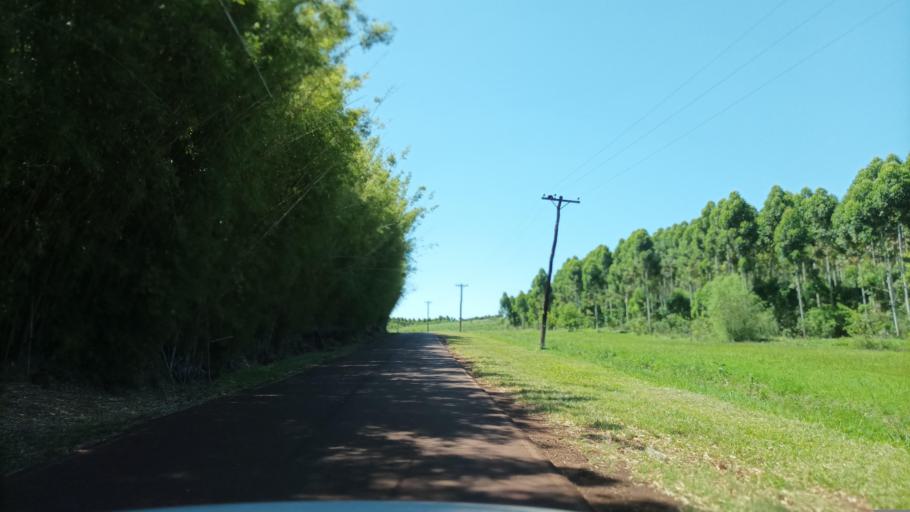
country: AR
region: Misiones
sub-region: Departamento de Apostoles
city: San Jose
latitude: -27.7825
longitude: -55.7223
